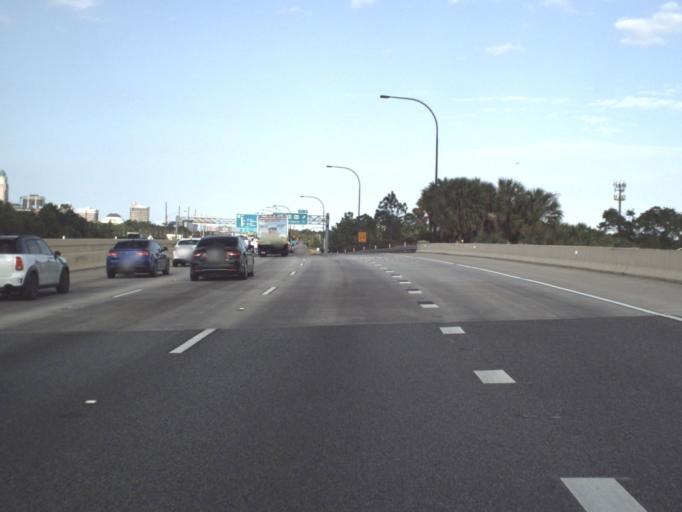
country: US
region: Florida
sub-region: Orange County
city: Orlando
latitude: 28.5351
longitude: -81.4019
